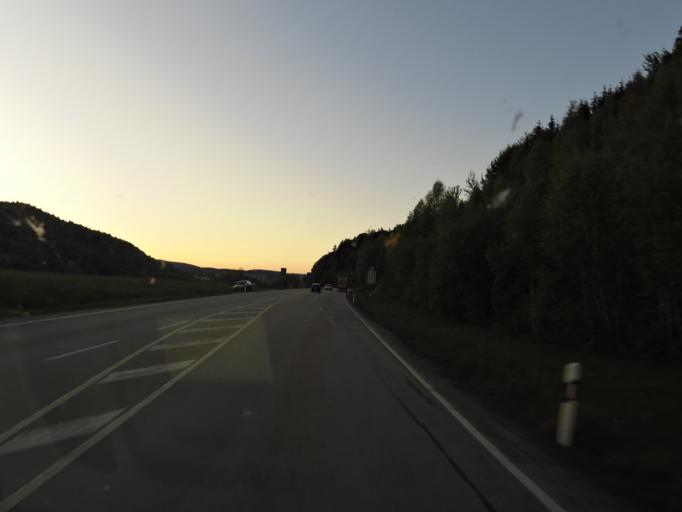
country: DE
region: Bavaria
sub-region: Lower Bavaria
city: Ringelai
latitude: 48.7923
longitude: 13.5059
